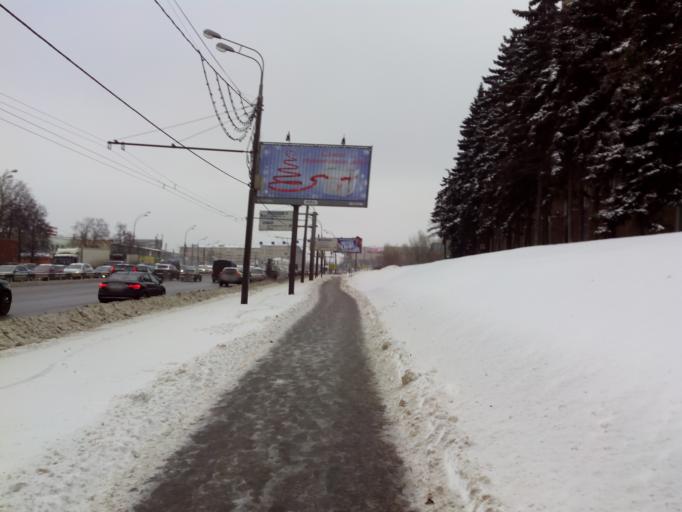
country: RU
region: Moscow
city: Kotlovka
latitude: 55.6770
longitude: 37.6252
